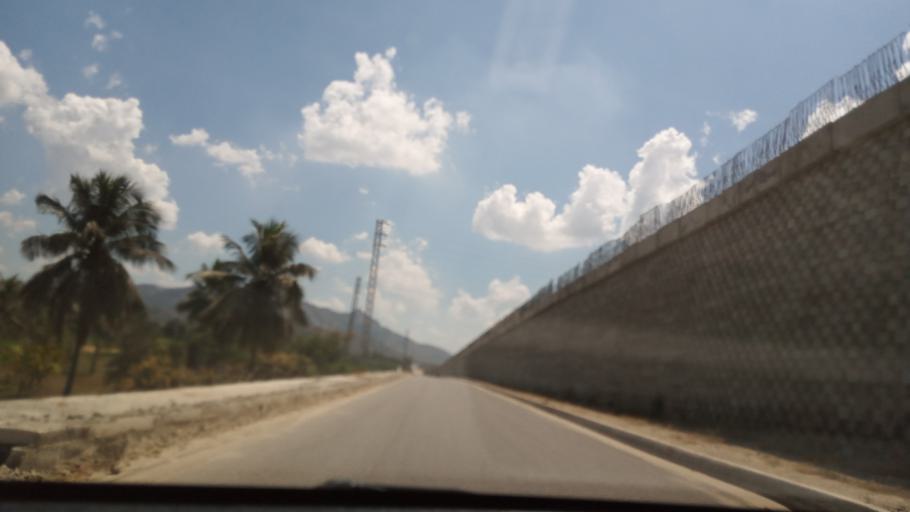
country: IN
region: Andhra Pradesh
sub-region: Chittoor
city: Pakala
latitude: 13.3541
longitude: 79.0854
